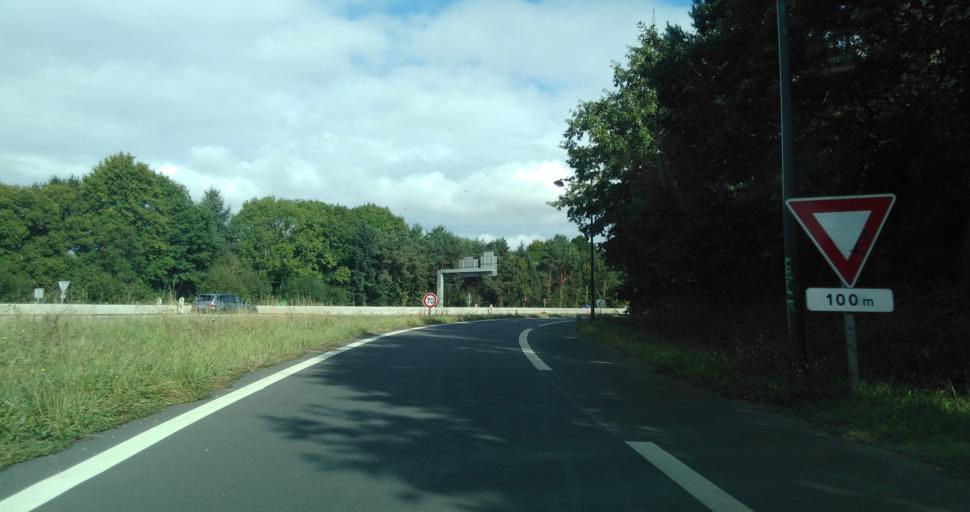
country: FR
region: Brittany
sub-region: Departement d'Ille-et-Vilaine
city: Montgermont
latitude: 48.1213
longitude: -1.7192
